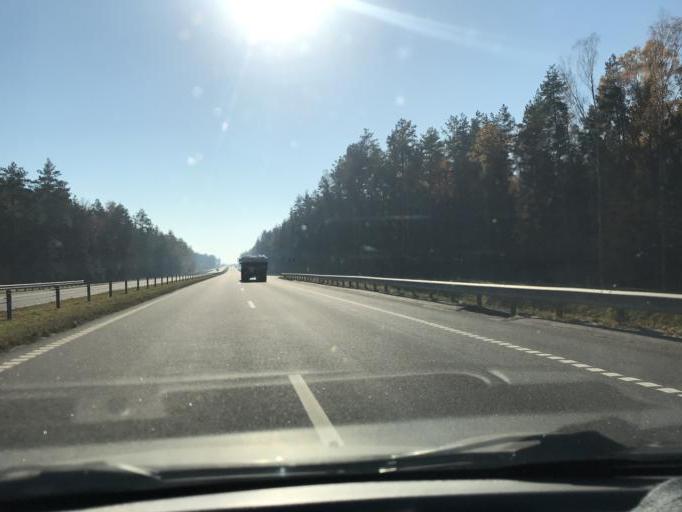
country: BY
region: Mogilev
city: Babruysk
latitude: 53.2101
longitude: 29.3449
